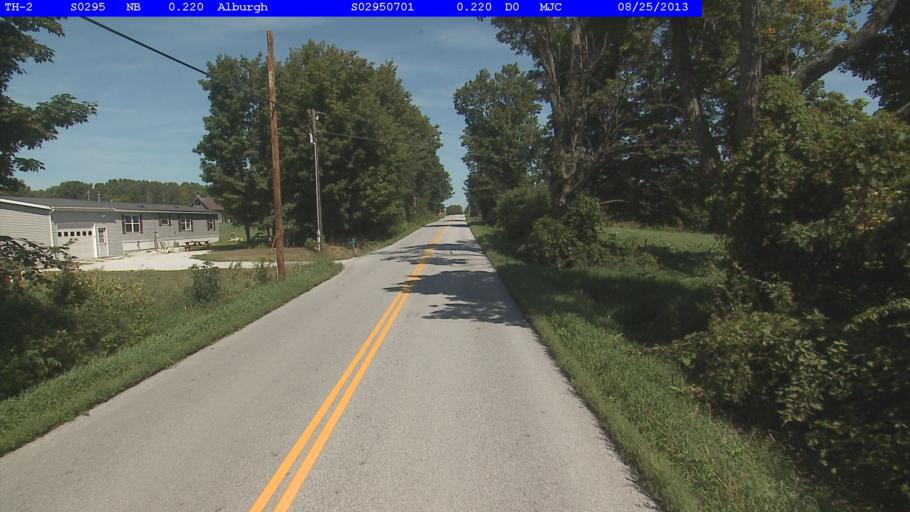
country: US
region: Vermont
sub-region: Franklin County
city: Swanton
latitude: 44.9778
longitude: -73.2309
